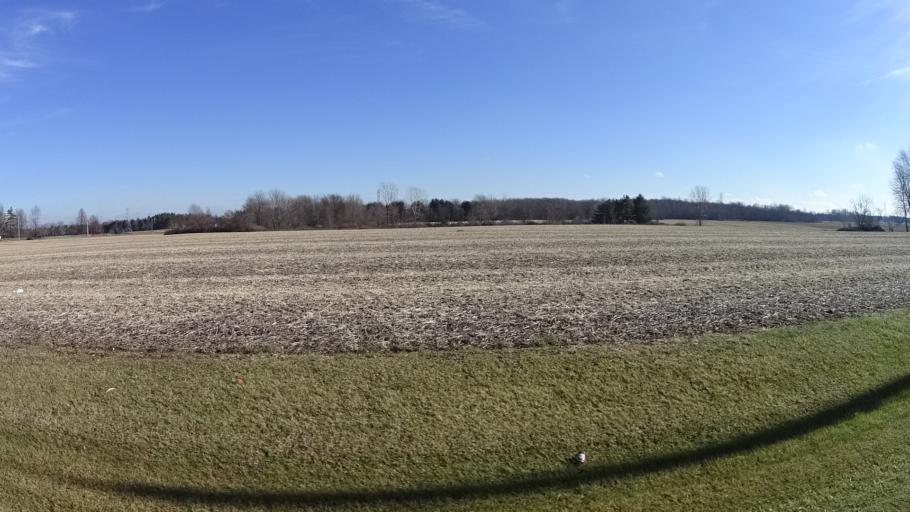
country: US
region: Ohio
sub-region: Lorain County
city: Wellington
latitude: 41.1274
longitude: -82.2785
